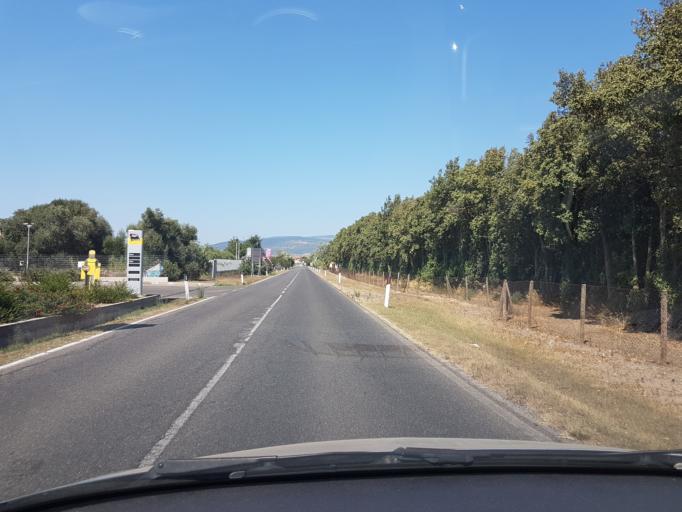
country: IT
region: Sardinia
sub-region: Provincia di Oristano
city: Riola Sardo
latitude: 39.9842
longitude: 8.5398
